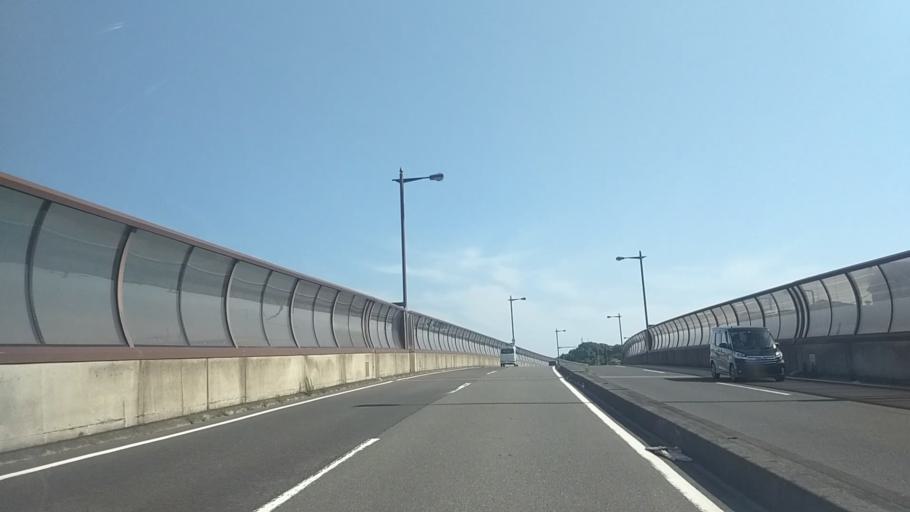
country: JP
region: Kanagawa
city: Fujisawa
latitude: 35.3411
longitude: 139.5024
